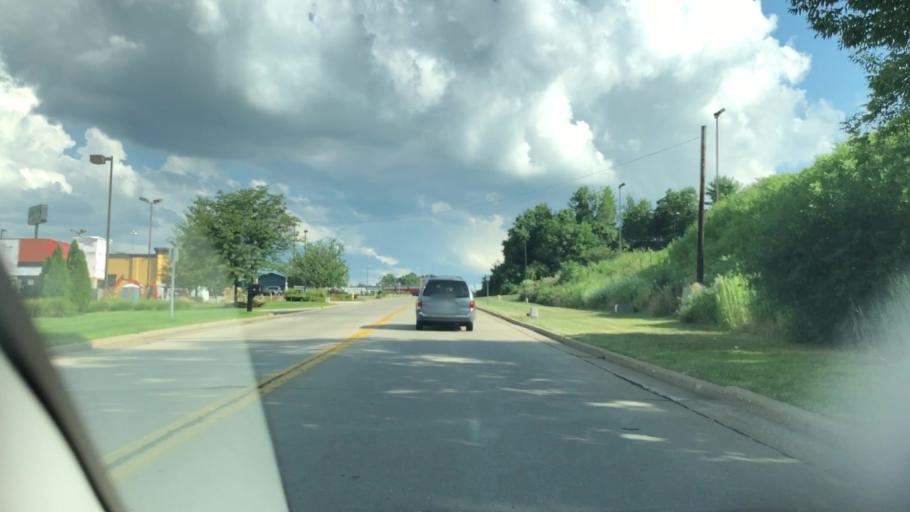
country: US
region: Ohio
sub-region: Summit County
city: Montrose-Ghent
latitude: 41.1347
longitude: -81.6543
